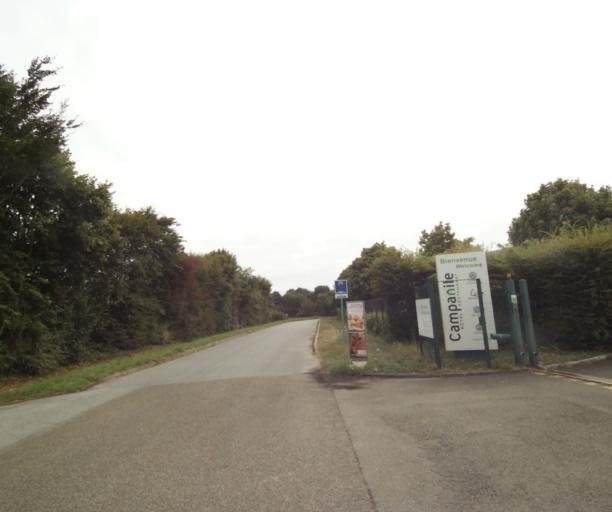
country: FR
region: Pays de la Loire
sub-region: Departement de la Sarthe
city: Solesmes
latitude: 47.8210
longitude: -0.2972
